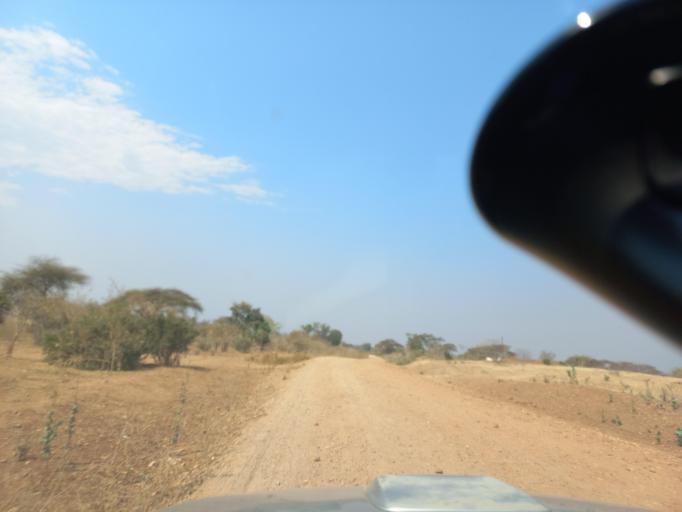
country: ZW
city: Chirundu
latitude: -15.9379
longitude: 28.8552
